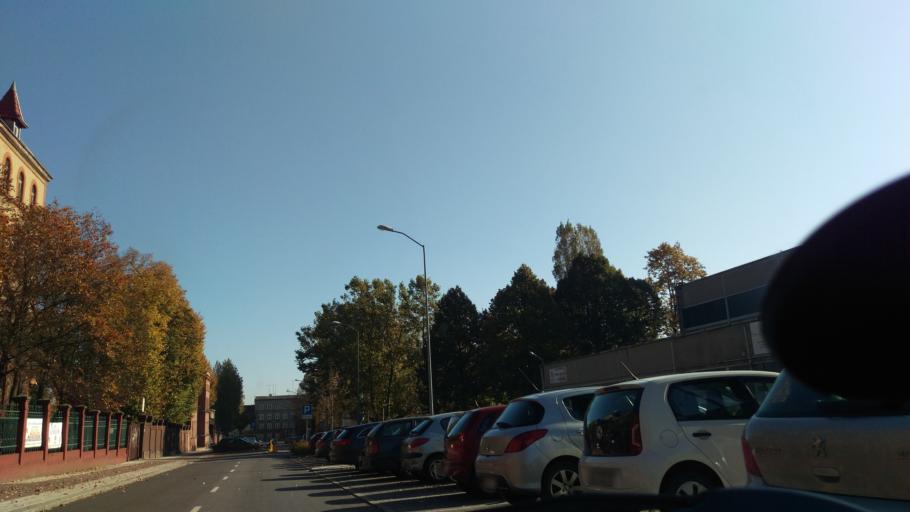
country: PL
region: West Pomeranian Voivodeship
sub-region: Szczecin
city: Szczecin
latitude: 53.4182
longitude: 14.5406
